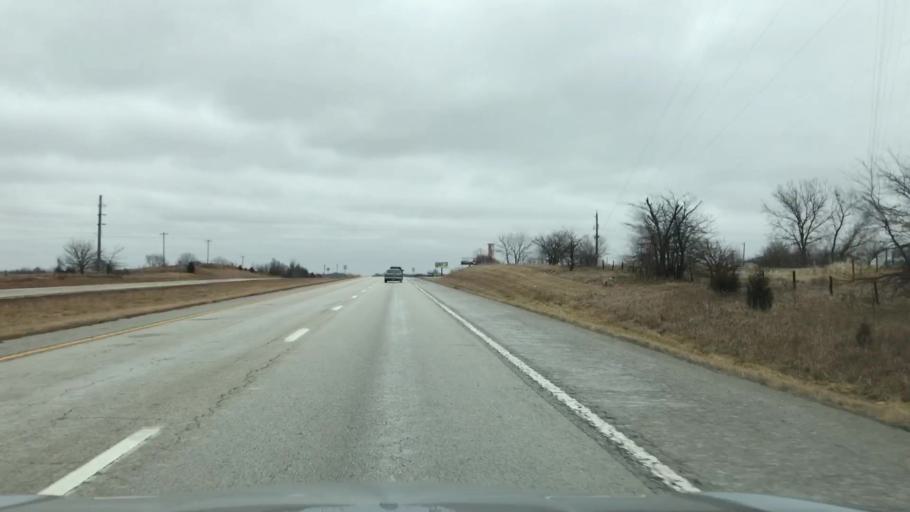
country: US
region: Missouri
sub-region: Clinton County
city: Cameron
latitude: 39.7522
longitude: -94.1887
